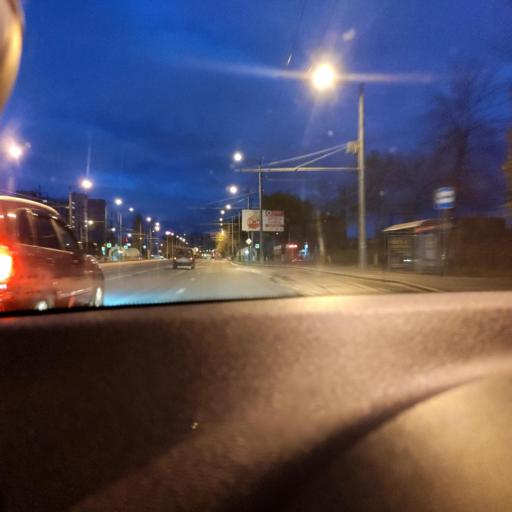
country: RU
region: Samara
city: Samara
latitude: 53.2380
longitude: 50.2034
